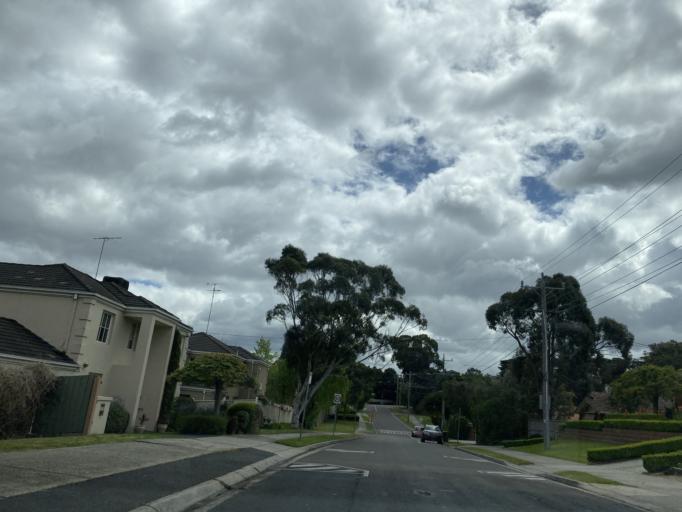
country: AU
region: Victoria
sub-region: Nillumbik
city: Eltham
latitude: -37.7552
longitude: 145.1436
